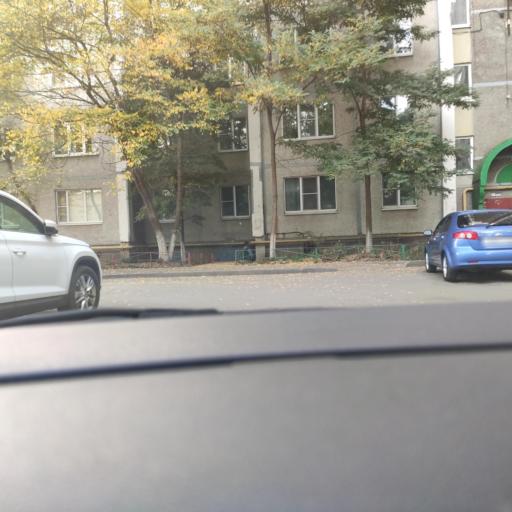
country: RU
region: Voronezj
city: Podgornoye
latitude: 51.7106
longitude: 39.1676
